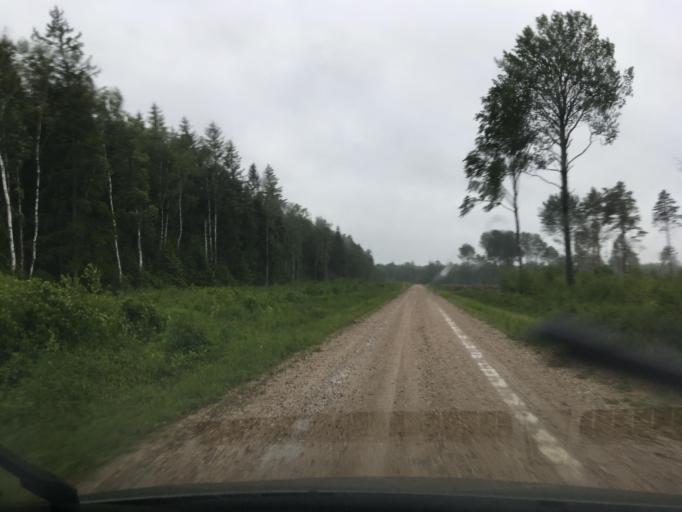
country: EE
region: Laeaene
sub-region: Lihula vald
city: Lihula
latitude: 58.6135
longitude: 23.8266
